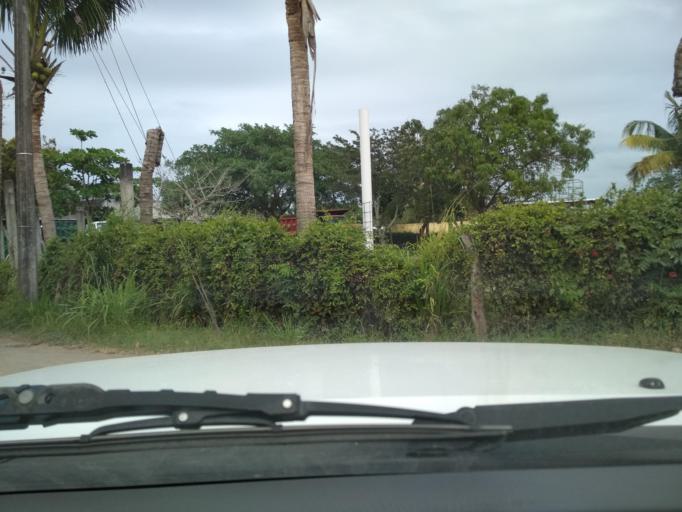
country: MX
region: Veracruz
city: El Tejar
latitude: 19.0656
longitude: -96.1358
